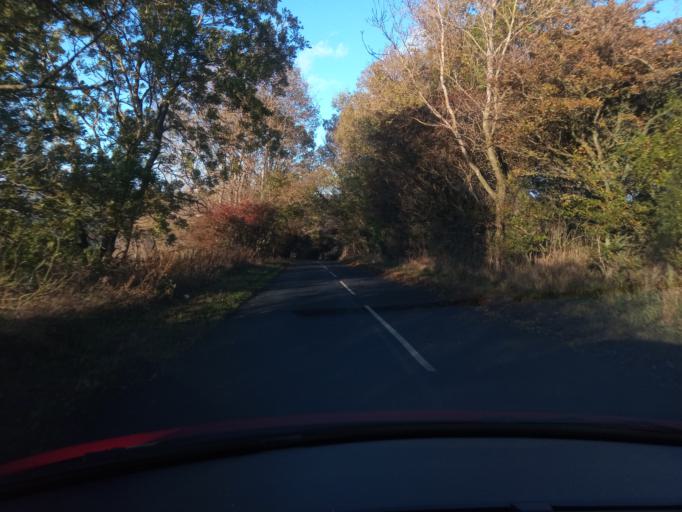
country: GB
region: England
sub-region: County Durham
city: Wolsingham
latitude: 54.7215
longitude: -1.8891
